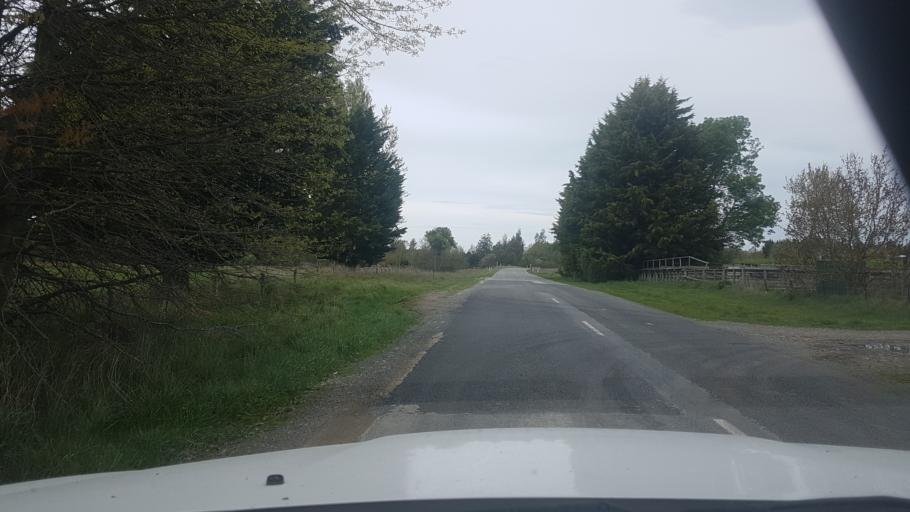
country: NZ
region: Canterbury
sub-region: Timaru District
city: Pleasant Point
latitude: -44.0790
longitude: 171.1768
